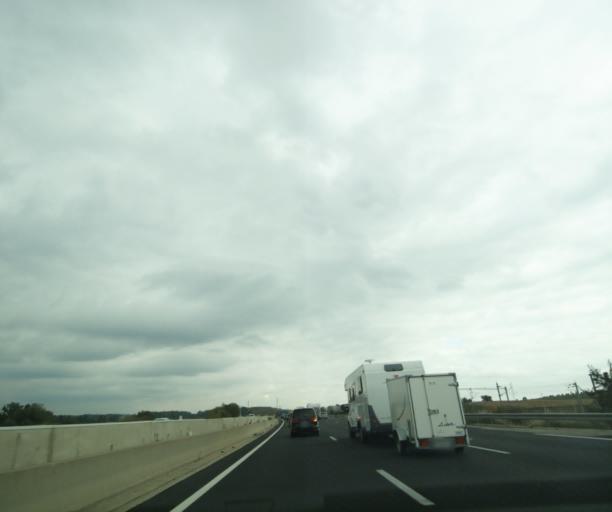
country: FR
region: Languedoc-Roussillon
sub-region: Departement de l'Herault
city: Lunel-Viel
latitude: 43.6973
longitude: 4.1055
